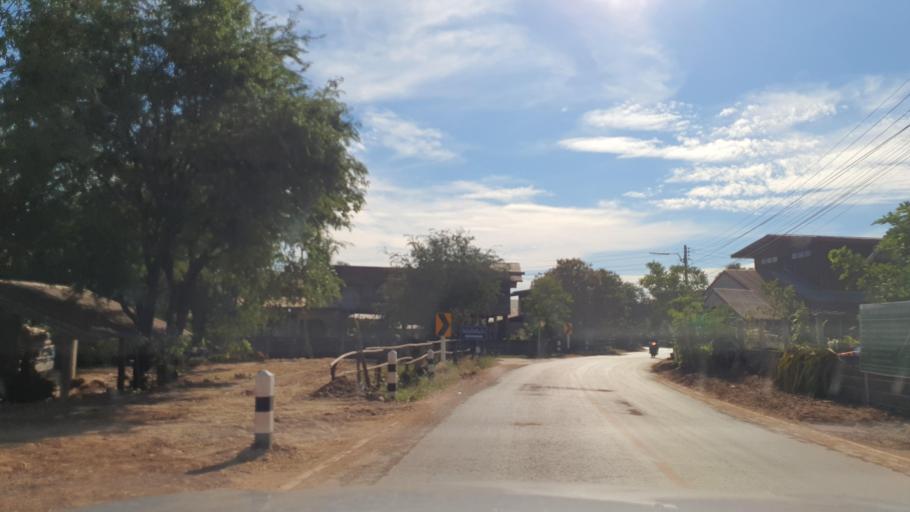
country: TH
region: Kalasin
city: Kuchinarai
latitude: 16.5927
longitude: 104.1326
